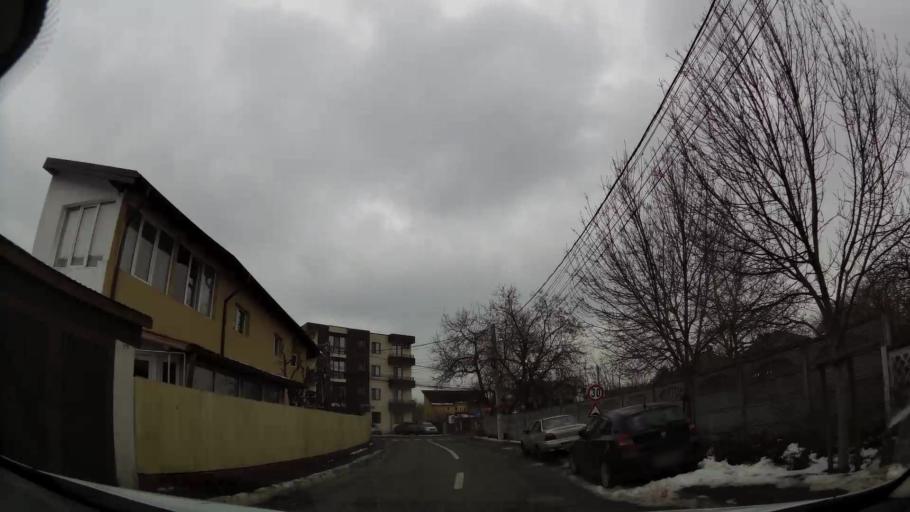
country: RO
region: Ilfov
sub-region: Comuna Otopeni
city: Otopeni
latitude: 44.5534
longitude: 26.0841
